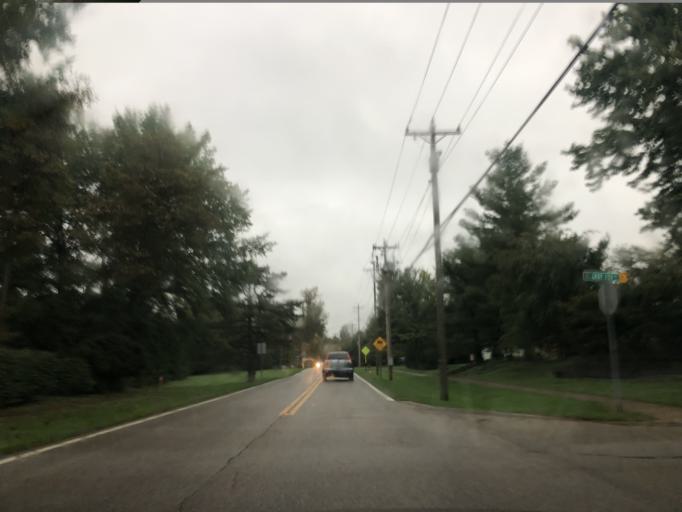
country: US
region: Ohio
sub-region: Clermont County
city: Mulberry
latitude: 39.2021
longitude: -84.2495
